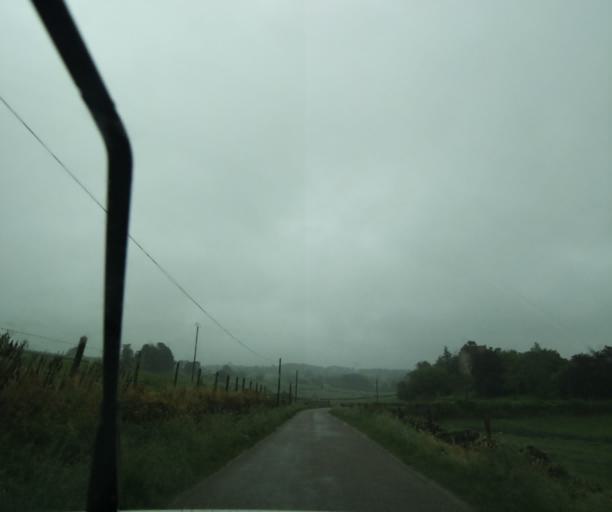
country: FR
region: Bourgogne
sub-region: Departement de Saone-et-Loire
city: Charolles
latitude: 46.3938
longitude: 4.2923
